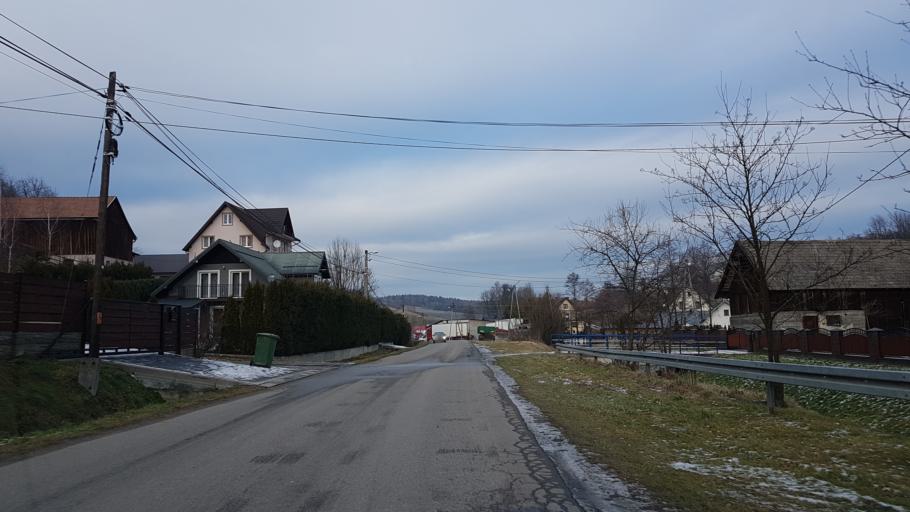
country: PL
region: Lesser Poland Voivodeship
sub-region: Powiat nowosadecki
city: Stary Sacz
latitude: 49.5367
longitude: 20.6110
